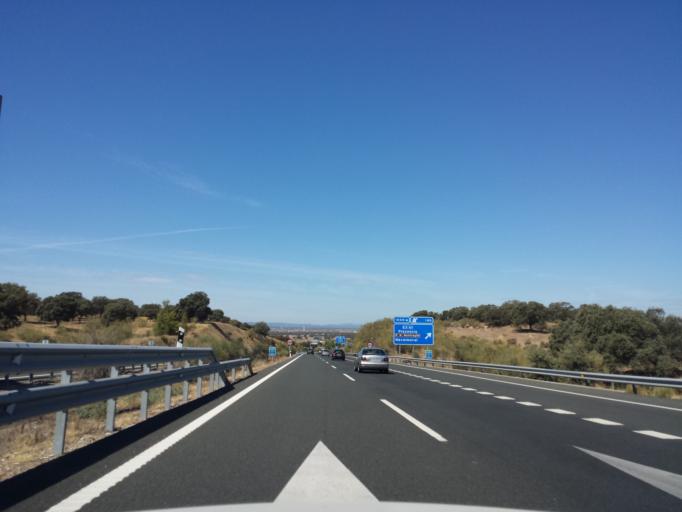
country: ES
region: Extremadura
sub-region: Provincia de Caceres
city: Millanes
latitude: 39.8720
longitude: -5.5729
